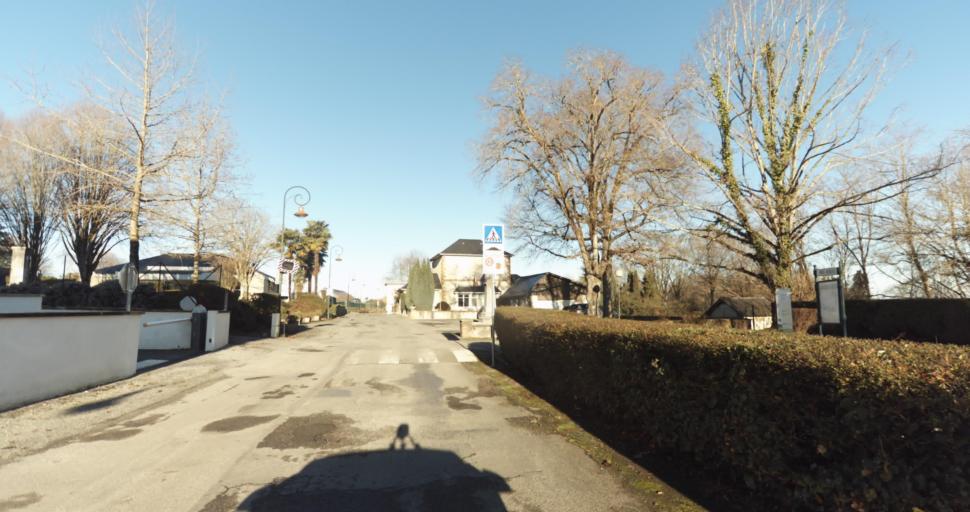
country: FR
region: Aquitaine
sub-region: Departement des Pyrenees-Atlantiques
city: Morlaas
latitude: 43.3269
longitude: -0.2582
